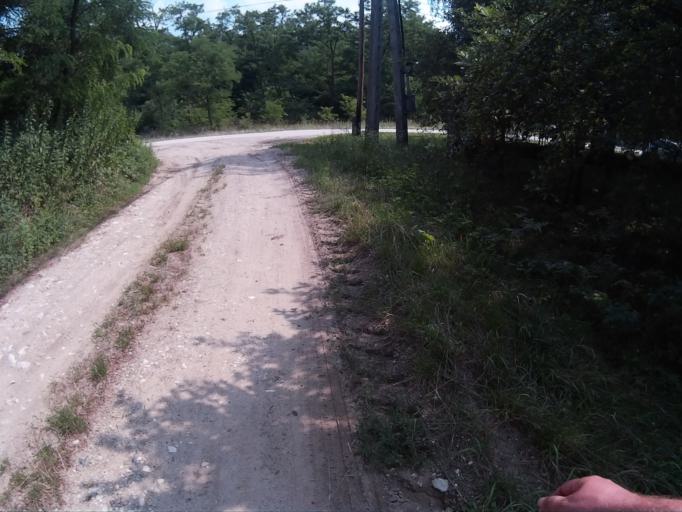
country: HU
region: Veszprem
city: Papa
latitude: 47.2958
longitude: 17.5966
